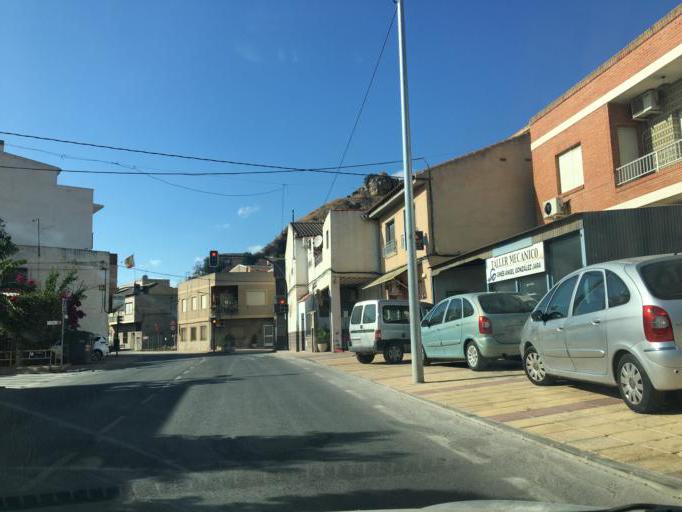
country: ES
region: Murcia
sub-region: Murcia
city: Murcia
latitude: 38.0224
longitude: -1.0879
